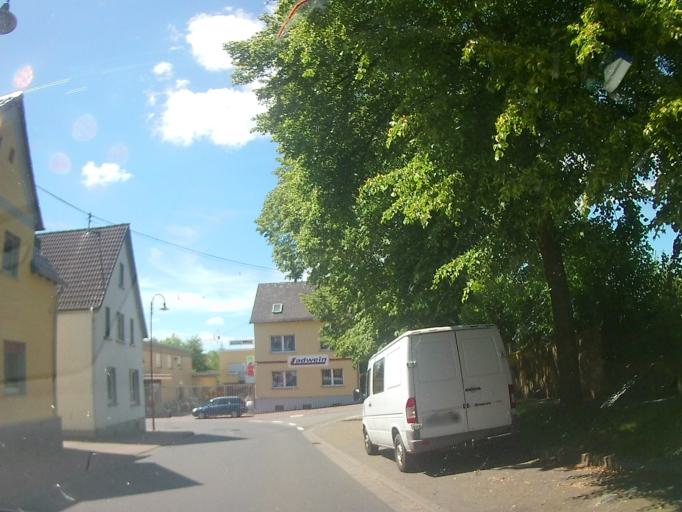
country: DE
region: Rheinland-Pfalz
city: Dierdorf
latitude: 50.5459
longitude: 7.6573
